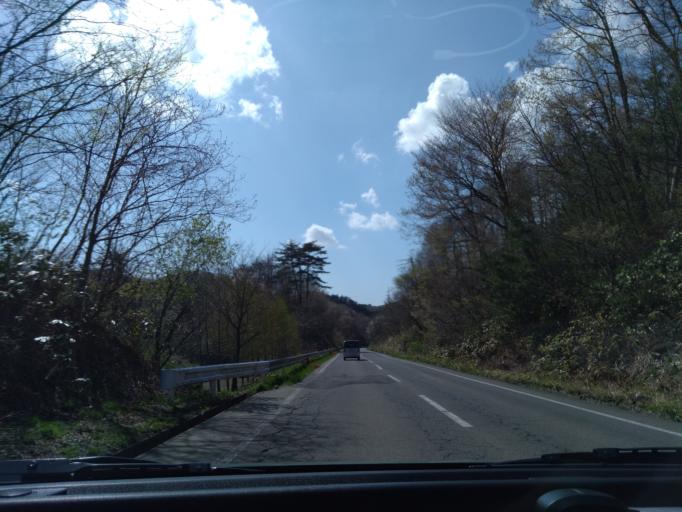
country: JP
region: Akita
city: Akita
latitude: 39.6937
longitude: 140.2428
